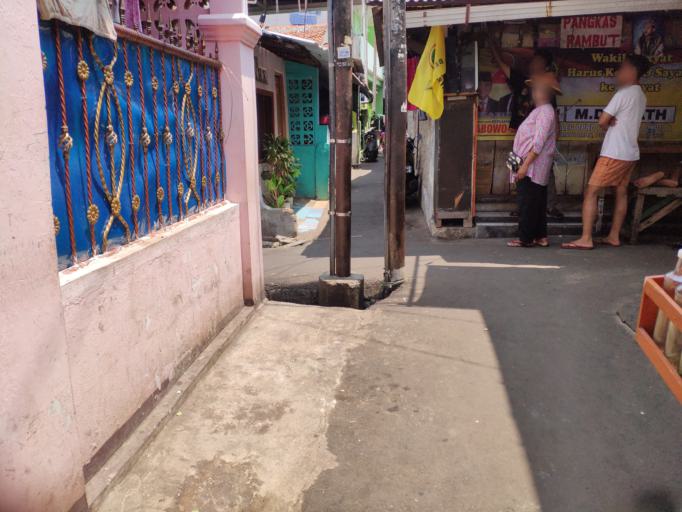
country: ID
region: Jakarta Raya
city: Jakarta
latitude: -6.2124
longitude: 106.8657
